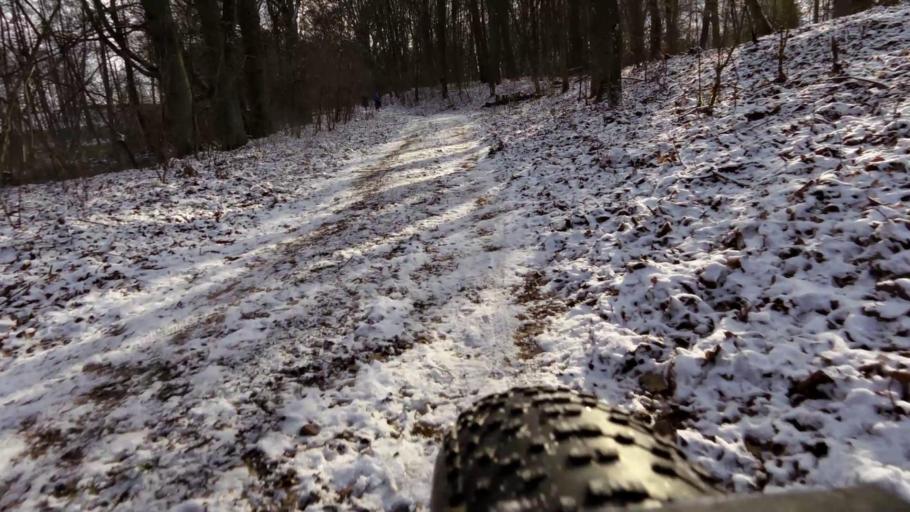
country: PL
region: West Pomeranian Voivodeship
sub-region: Powiat walecki
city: Tuczno
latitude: 53.3032
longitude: 16.2730
